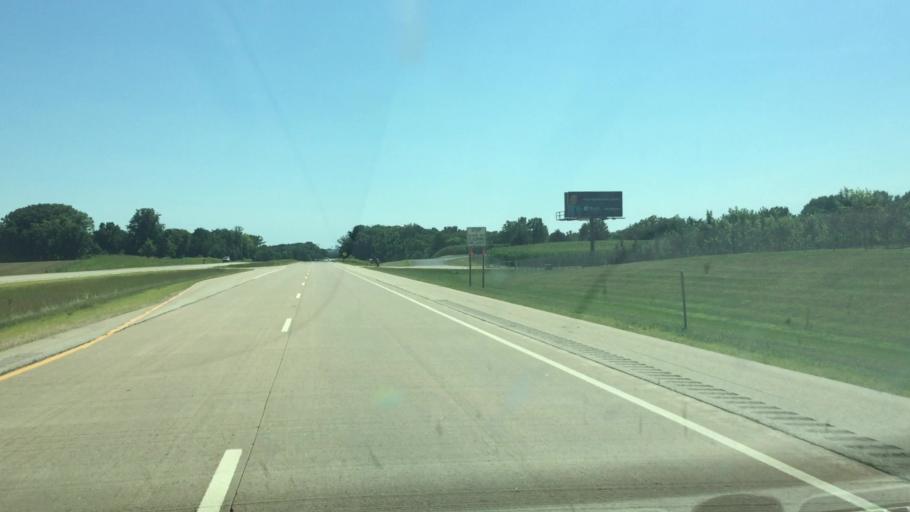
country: US
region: Wisconsin
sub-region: Grant County
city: Platteville
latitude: 42.6884
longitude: -90.5329
